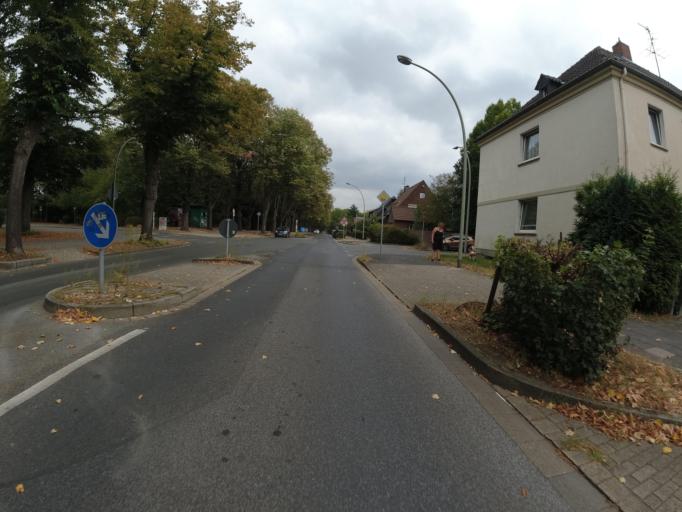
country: DE
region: North Rhine-Westphalia
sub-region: Regierungsbezirk Dusseldorf
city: Moers
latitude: 51.4569
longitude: 6.6956
